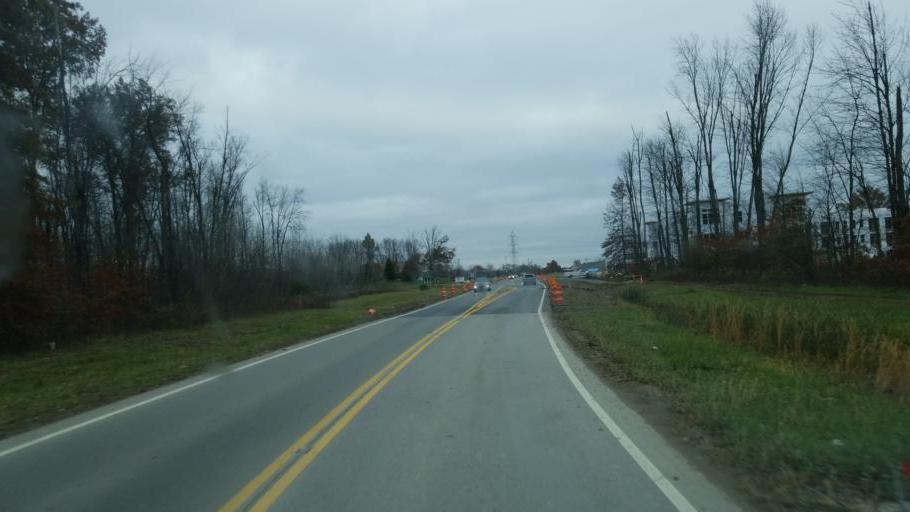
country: US
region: Ohio
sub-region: Franklin County
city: New Albany
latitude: 40.0876
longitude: -82.8540
